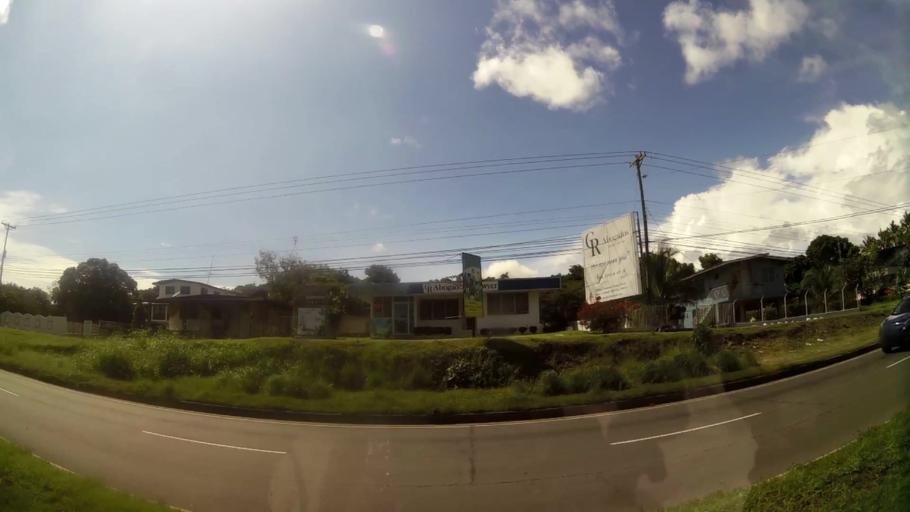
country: PA
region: Panama
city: Chame
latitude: 8.5778
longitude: -79.8844
